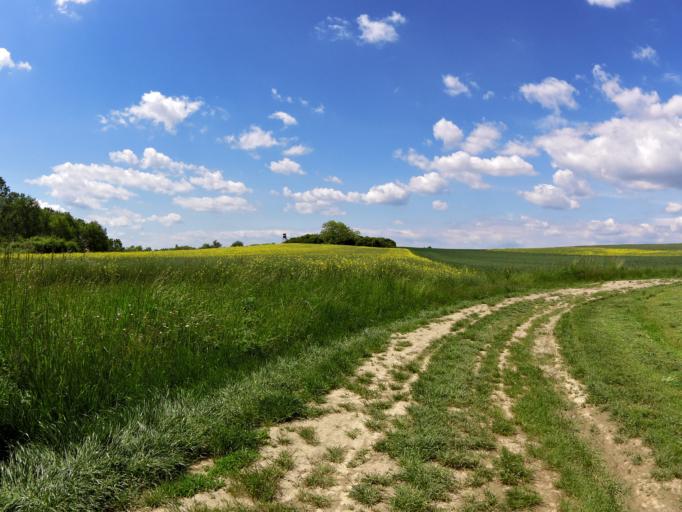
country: DE
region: Bavaria
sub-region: Regierungsbezirk Unterfranken
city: Sommerhausen
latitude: 49.7247
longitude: 10.0415
